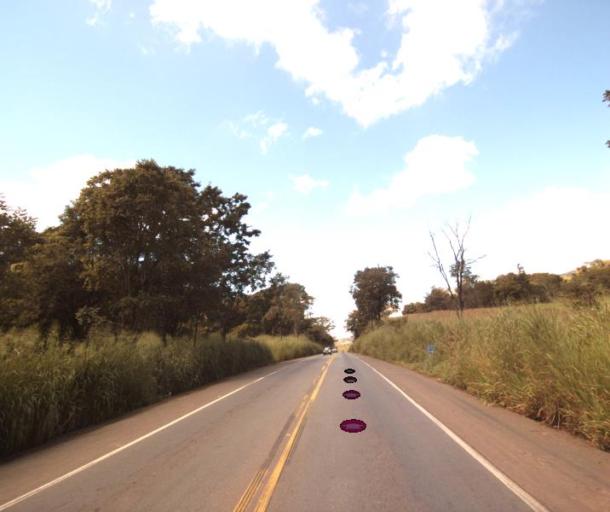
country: BR
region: Goias
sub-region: Jaragua
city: Jaragua
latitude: -15.7940
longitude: -49.3014
